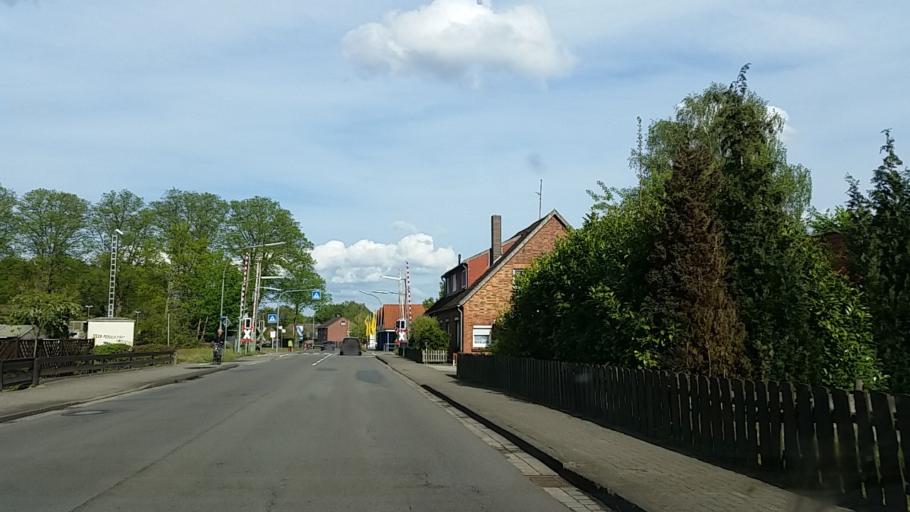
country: DE
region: Lower Saxony
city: Bodenteich
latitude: 52.8328
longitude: 10.6732
